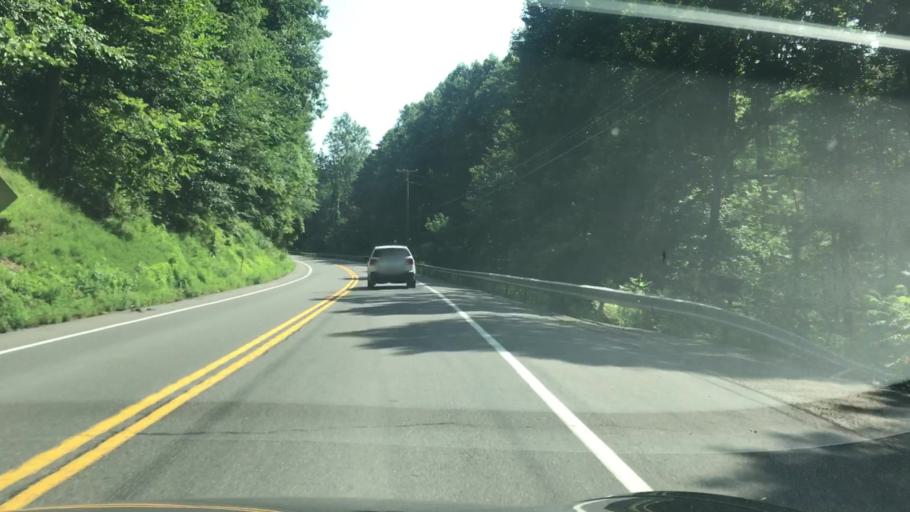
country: US
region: Pennsylvania
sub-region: Lycoming County
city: Garden View
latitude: 41.4249
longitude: -77.0152
